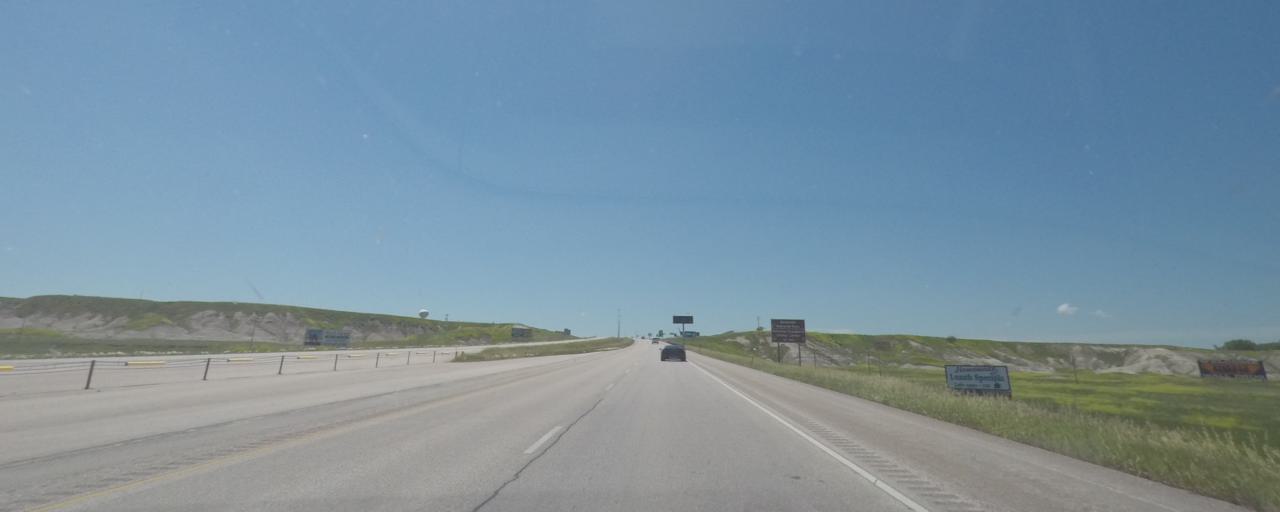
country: US
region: South Dakota
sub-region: Haakon County
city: Philip
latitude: 43.9877
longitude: -102.2248
